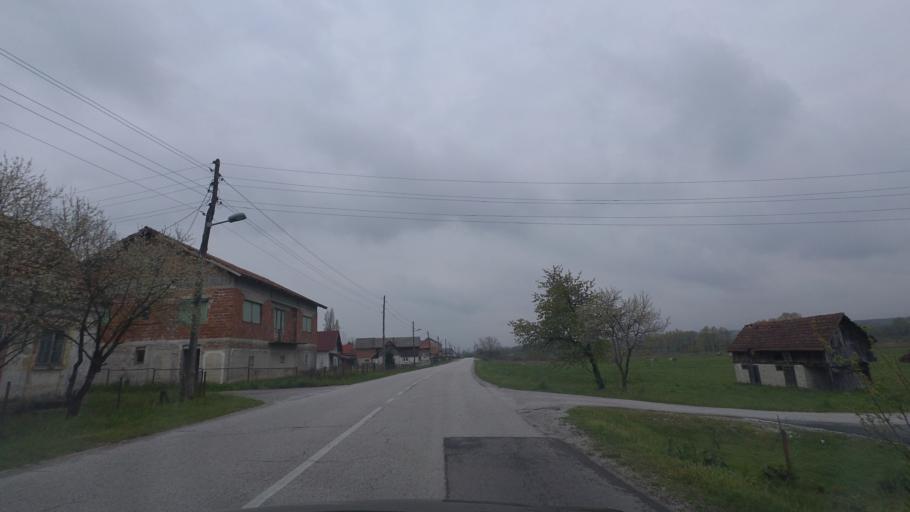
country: HR
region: Zagrebacka
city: Jastrebarsko
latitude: 45.6160
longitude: 15.5803
